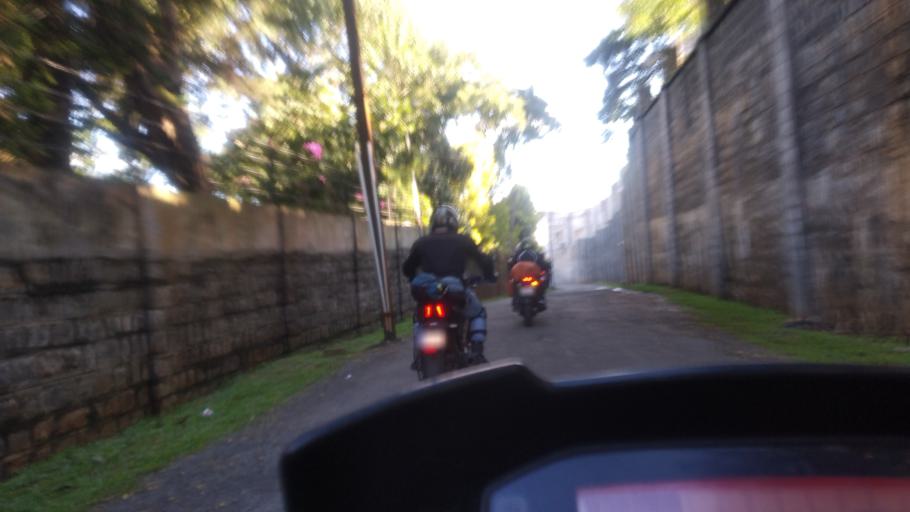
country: IN
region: Tamil Nadu
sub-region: Salem
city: Salem
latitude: 11.7718
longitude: 78.2108
